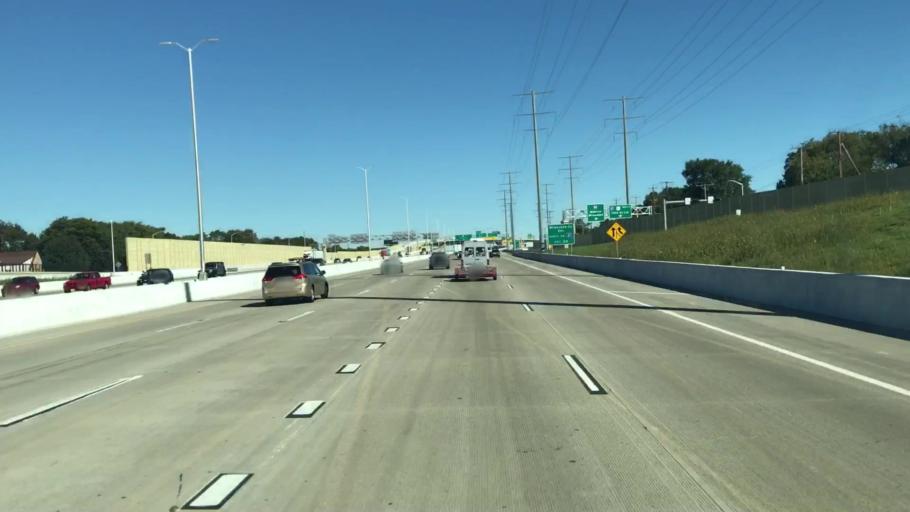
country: US
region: Wisconsin
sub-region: Milwaukee County
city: West Allis
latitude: 43.0171
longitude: -88.0362
